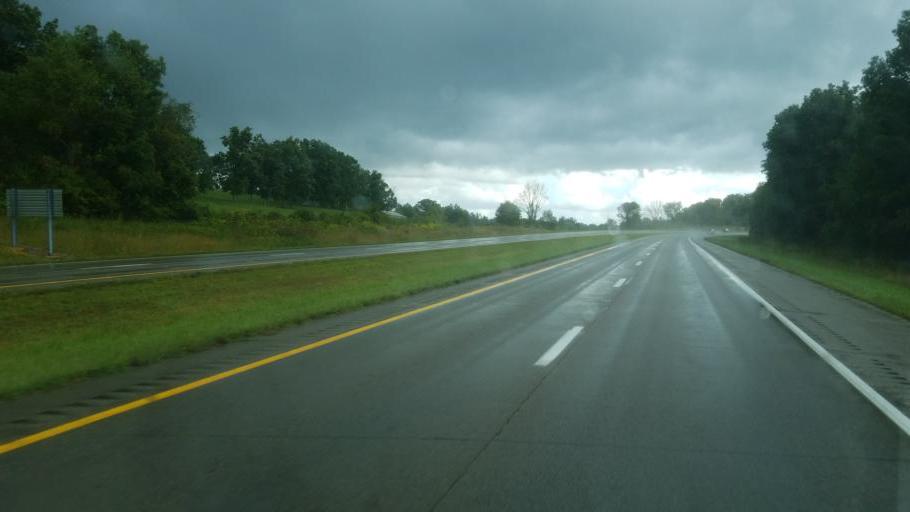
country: US
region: Ohio
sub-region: Jackson County
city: Jackson
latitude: 39.0198
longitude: -82.6429
